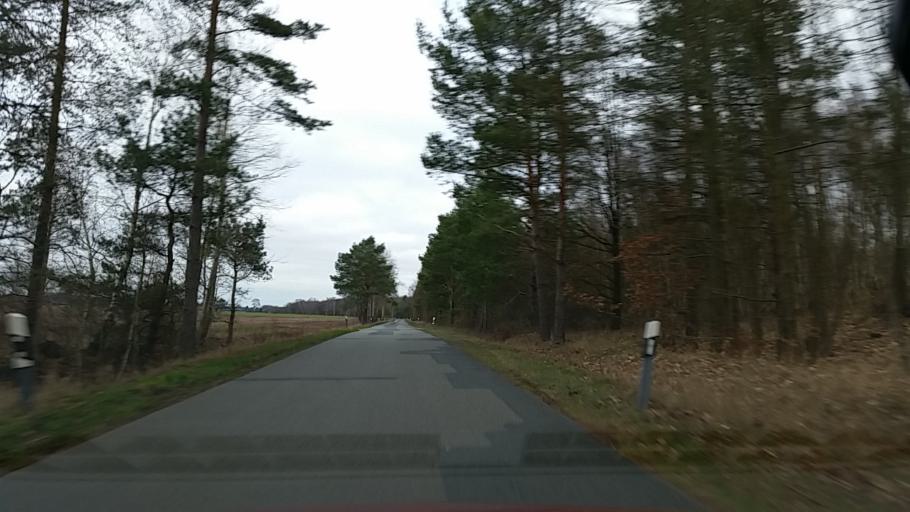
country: DE
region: Lower Saxony
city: Luder
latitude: 52.7916
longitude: 10.6702
